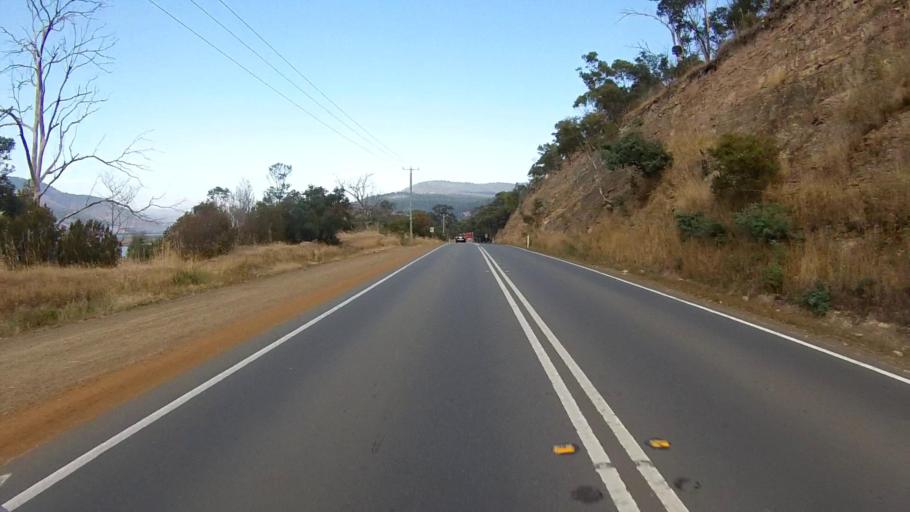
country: AU
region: Tasmania
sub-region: Brighton
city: Bridgewater
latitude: -42.7251
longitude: 147.1980
